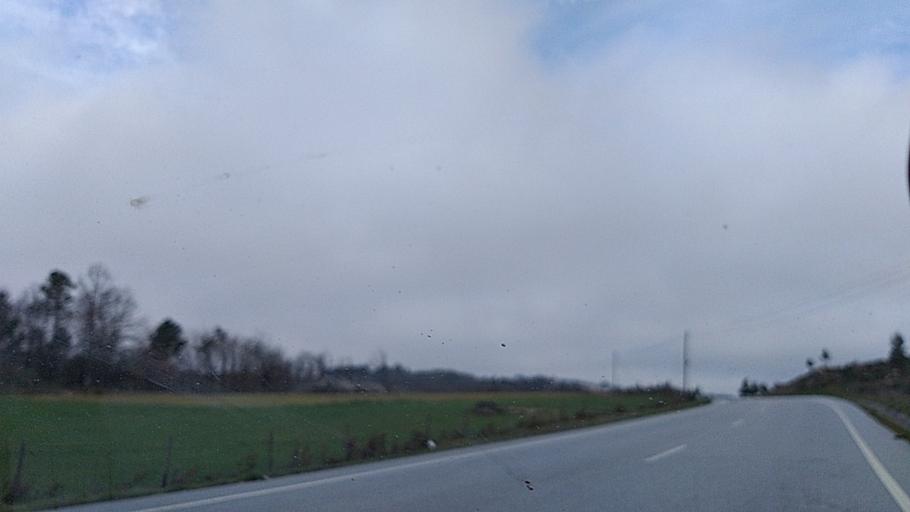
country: PT
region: Guarda
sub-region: Fornos de Algodres
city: Fornos de Algodres
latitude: 40.6711
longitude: -7.4740
